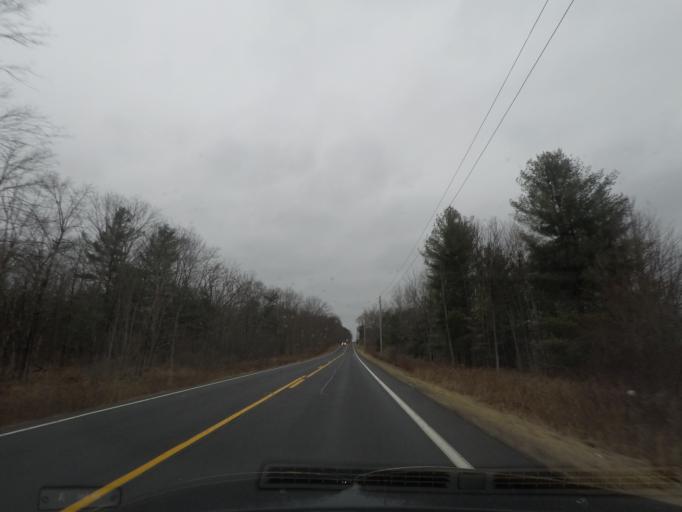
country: US
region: New York
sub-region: Rensselaer County
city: East Greenbush
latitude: 42.6080
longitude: -73.6604
